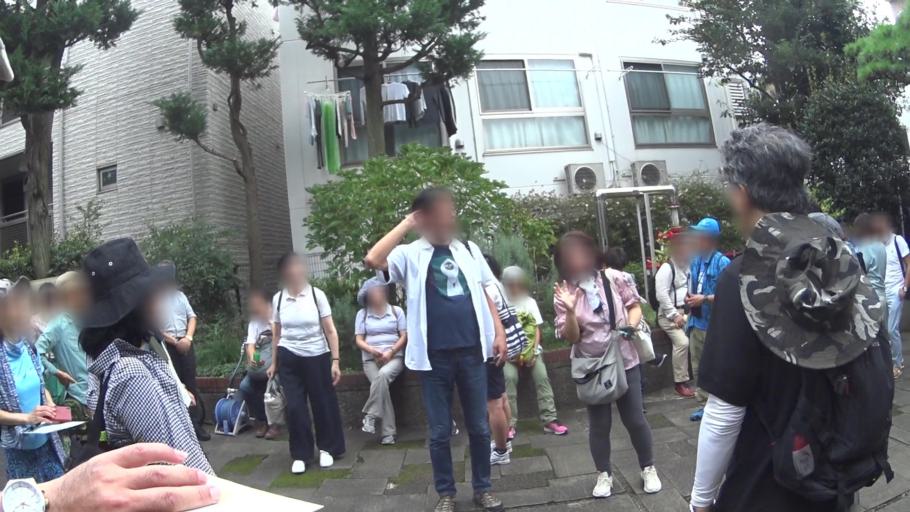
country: JP
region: Tokyo
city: Tokyo
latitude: 35.7209
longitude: 139.7205
